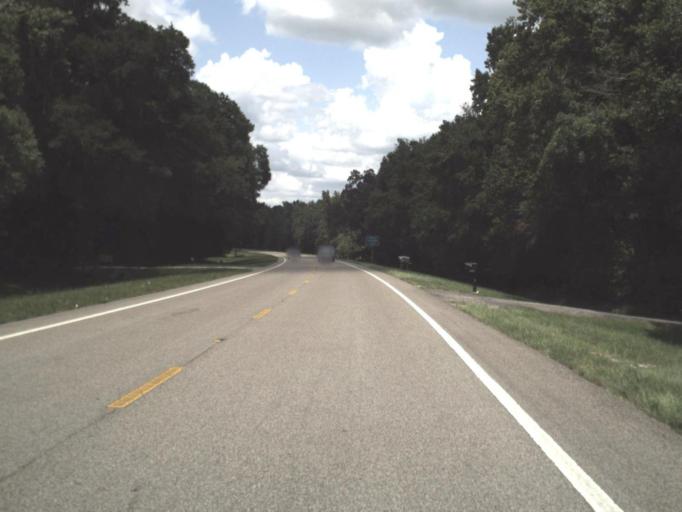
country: US
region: Florida
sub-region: Hernando County
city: North Brooksville
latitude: 28.6047
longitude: -82.4009
